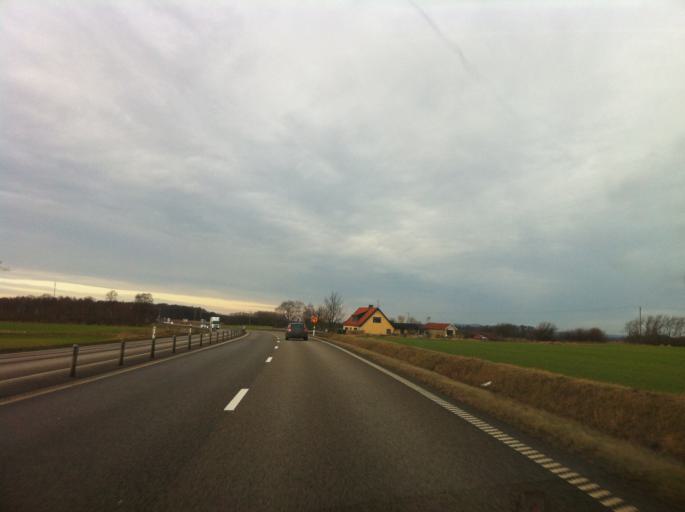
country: DK
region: Capital Region
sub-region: Helsingor Kommune
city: Helsingor
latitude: 56.1168
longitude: 12.6308
